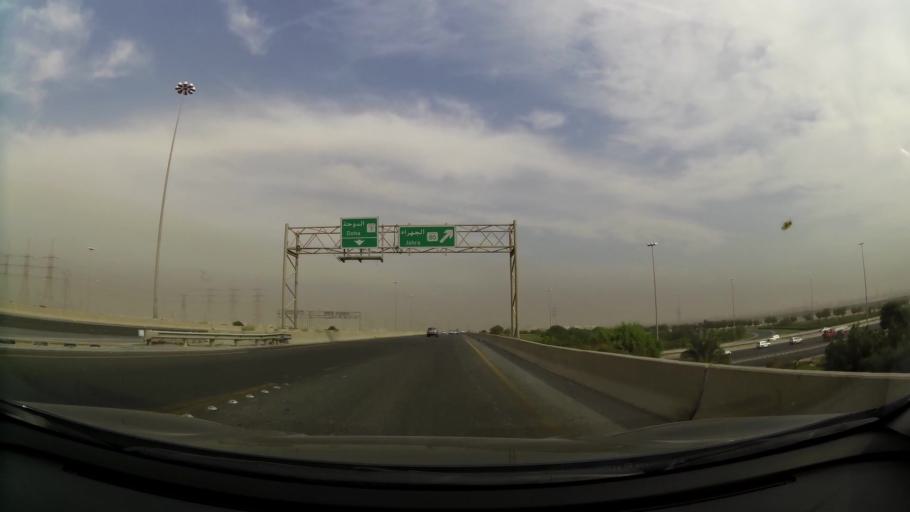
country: KW
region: Muhafazat al Jahra'
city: Al Jahra'
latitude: 29.3108
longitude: 47.7854
